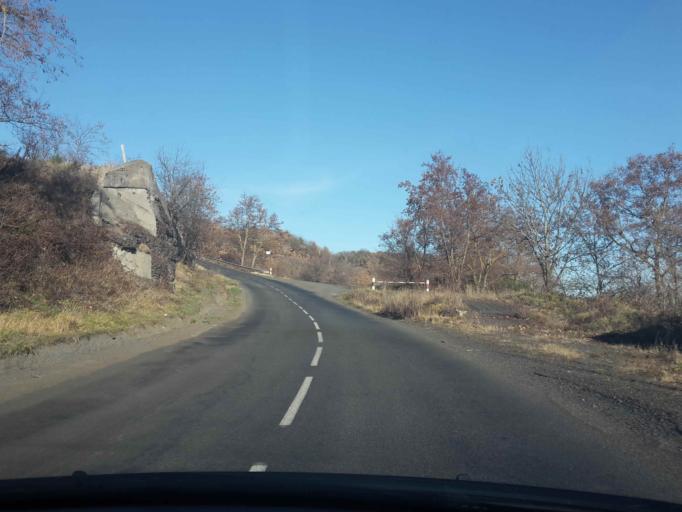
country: FR
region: Auvergne
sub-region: Departement du Cantal
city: Massiac
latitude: 45.2594
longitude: 3.1800
